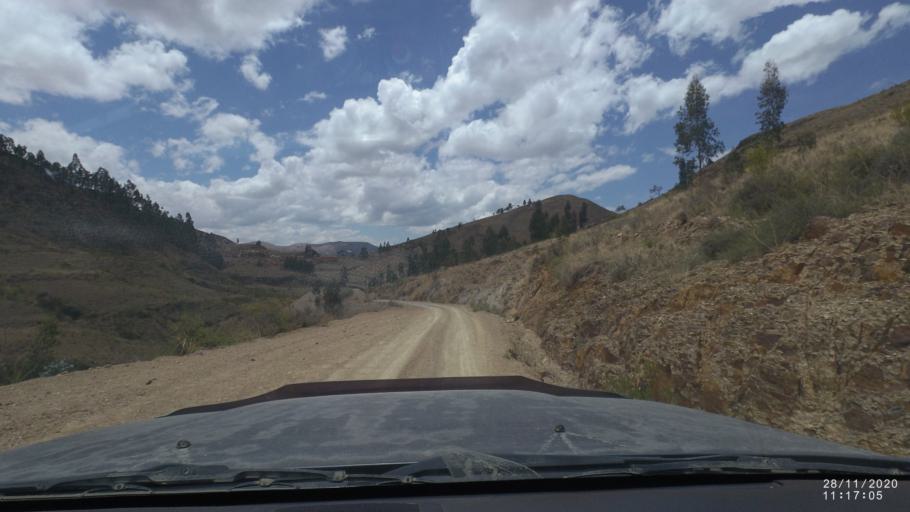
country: BO
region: Cochabamba
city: Tarata
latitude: -17.7507
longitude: -66.0792
